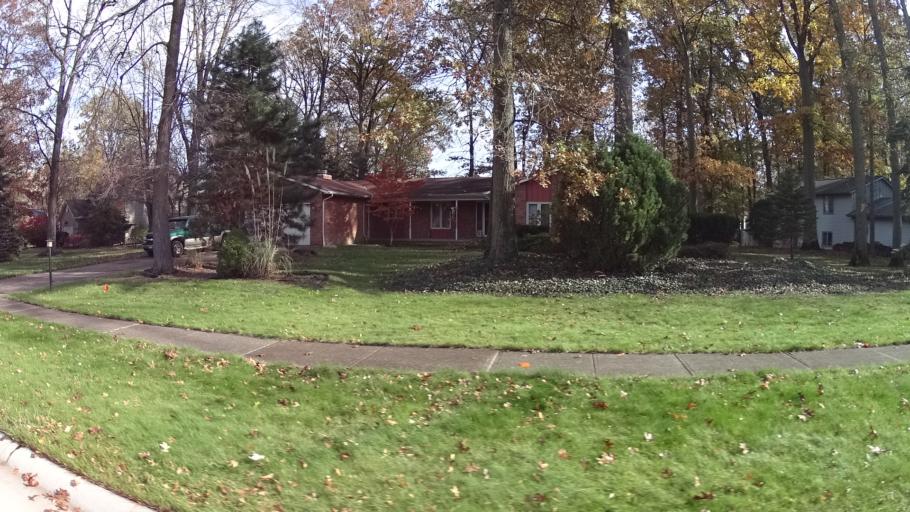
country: US
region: Ohio
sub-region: Lorain County
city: Avon Lake
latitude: 41.5005
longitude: -82.0224
